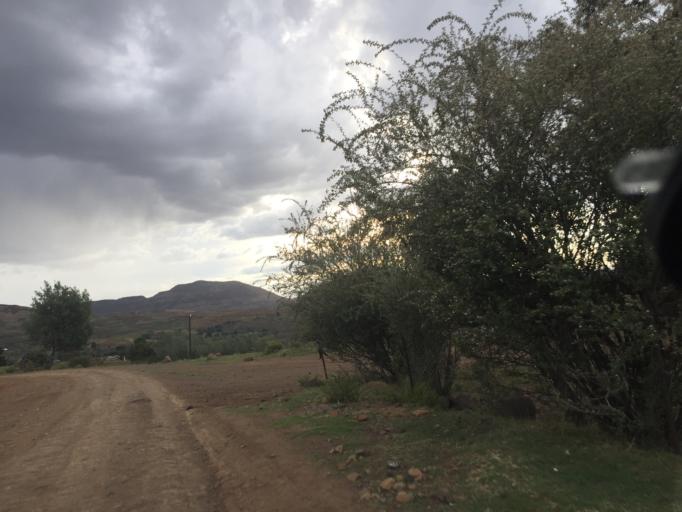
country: LS
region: Leribe
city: Leribe
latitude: -29.1556
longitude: 28.0357
